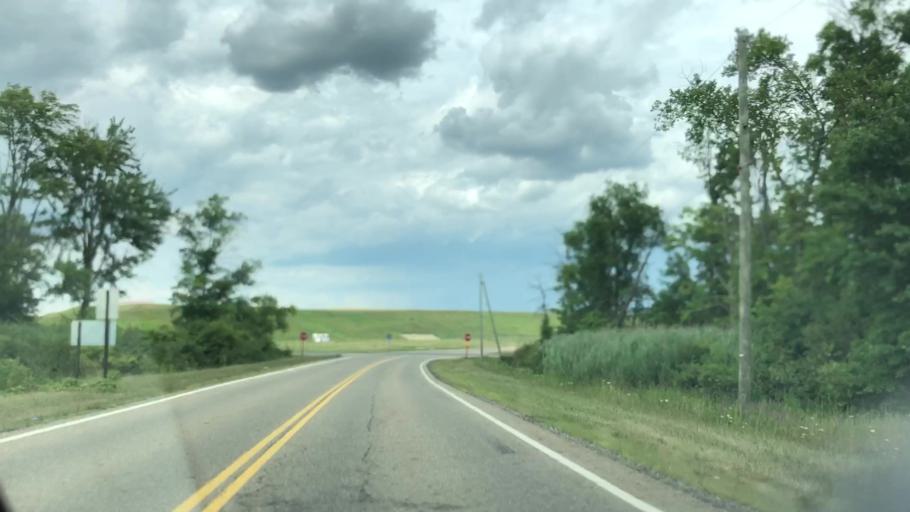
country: US
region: Ohio
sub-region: Summit County
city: Greensburg
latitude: 40.8994
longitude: -81.4590
